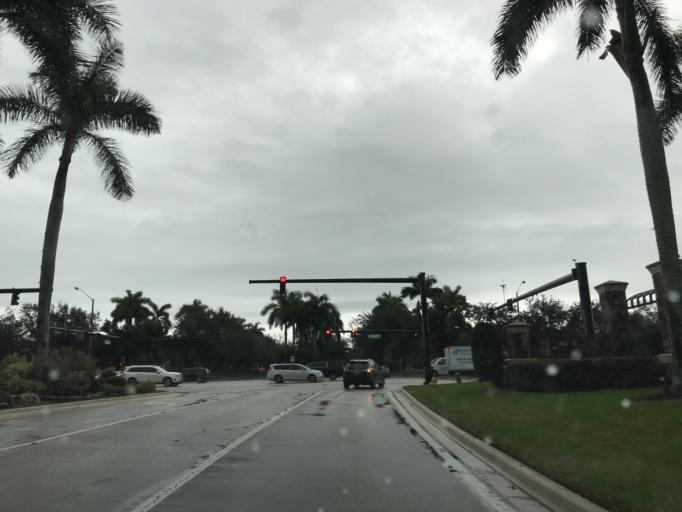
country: US
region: Florida
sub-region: Broward County
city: Coral Springs
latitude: 26.3087
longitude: -80.2795
